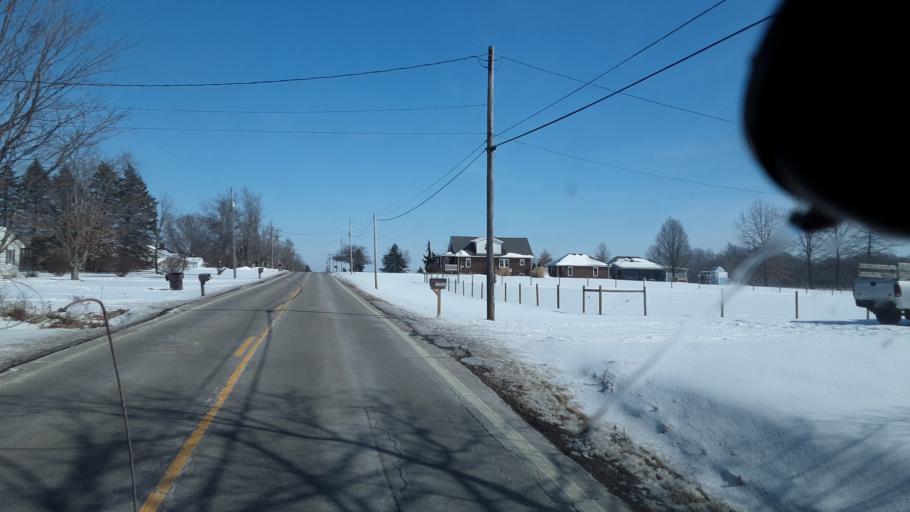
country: US
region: Ohio
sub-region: Columbiana County
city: Salem
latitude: 40.9447
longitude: -80.9015
